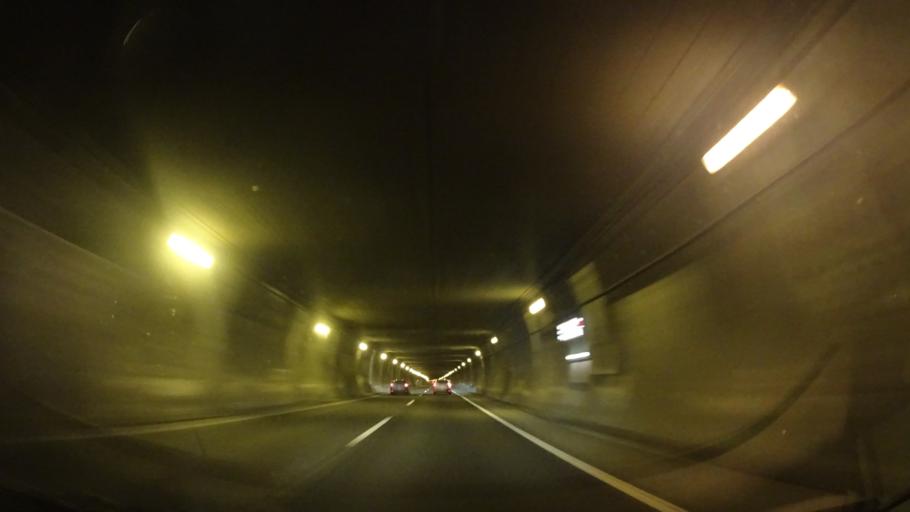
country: ES
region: Castille and Leon
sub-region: Provincia de Leon
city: Sena de Luna
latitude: 42.9718
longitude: -5.8349
